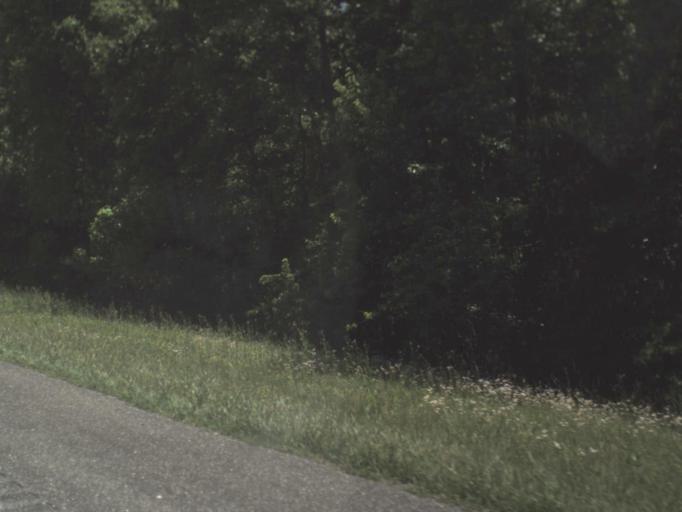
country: US
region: Florida
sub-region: Jefferson County
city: Monticello
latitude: 30.4864
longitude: -83.9530
